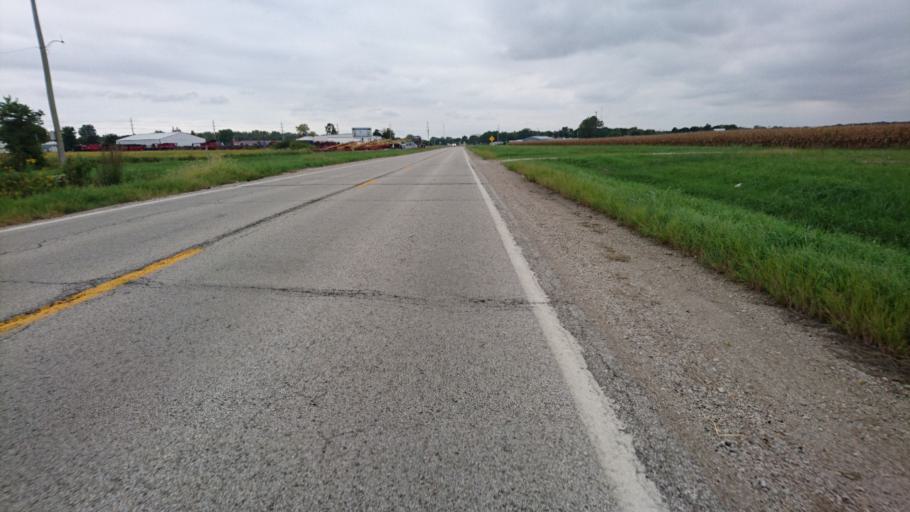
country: US
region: Illinois
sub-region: Livingston County
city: Pontiac
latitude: 40.8954
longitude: -88.6297
